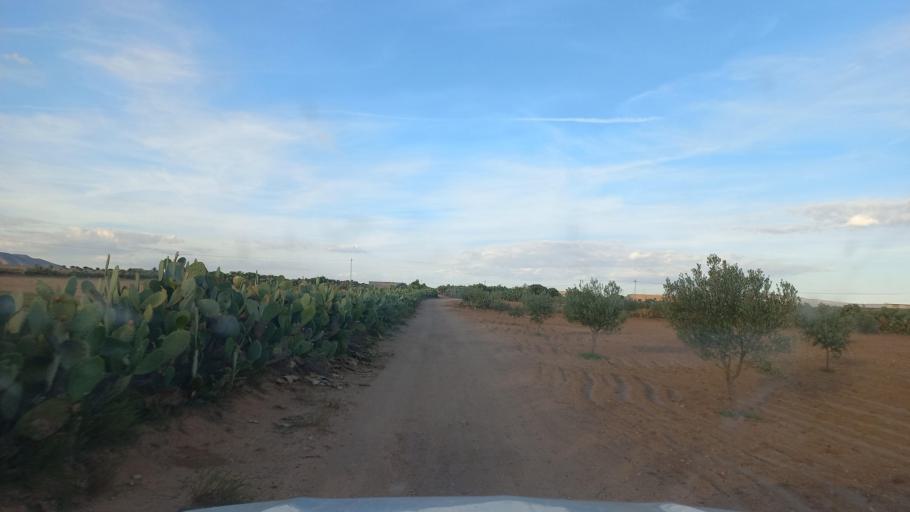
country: TN
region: Al Qasrayn
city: Sbiba
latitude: 35.3538
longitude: 9.0321
